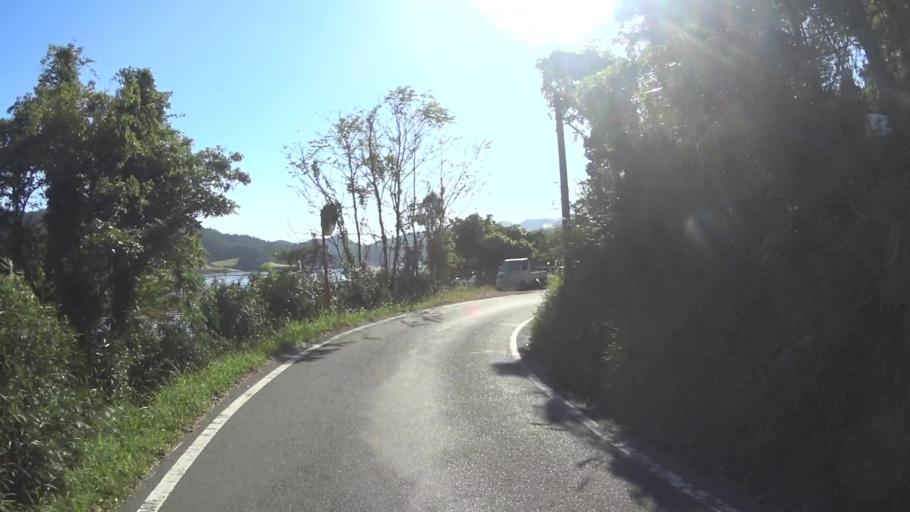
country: JP
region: Hyogo
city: Toyooka
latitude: 35.6399
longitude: 134.8959
